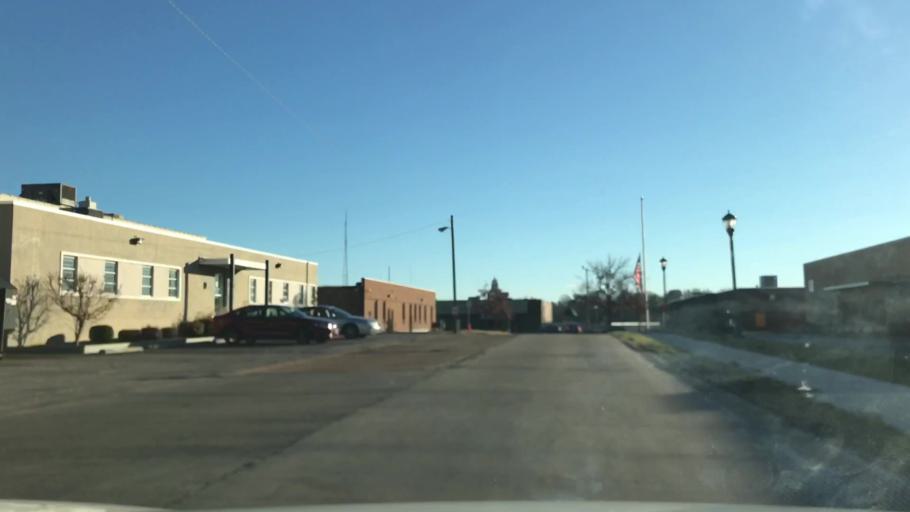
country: US
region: Missouri
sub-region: Saint Louis County
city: Brentwood
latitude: 38.6253
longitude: -90.3397
